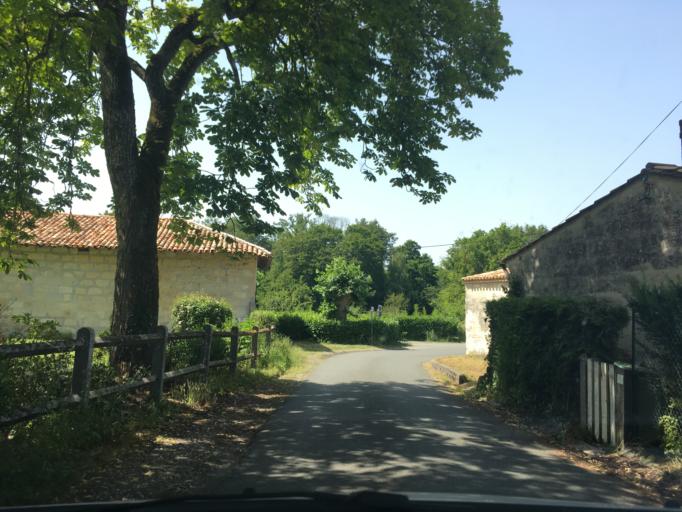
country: FR
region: Aquitaine
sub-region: Departement de la Gironde
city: Cantenac
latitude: 45.0141
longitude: -0.6409
